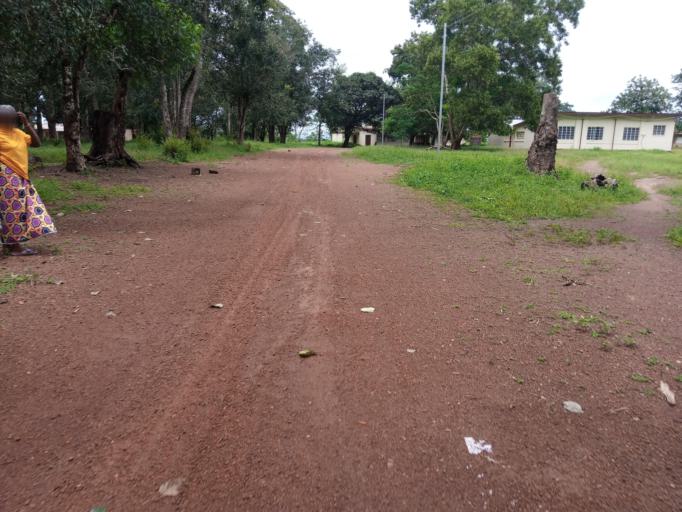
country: SL
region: Southern Province
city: Largo
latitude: 8.1984
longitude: -12.0622
